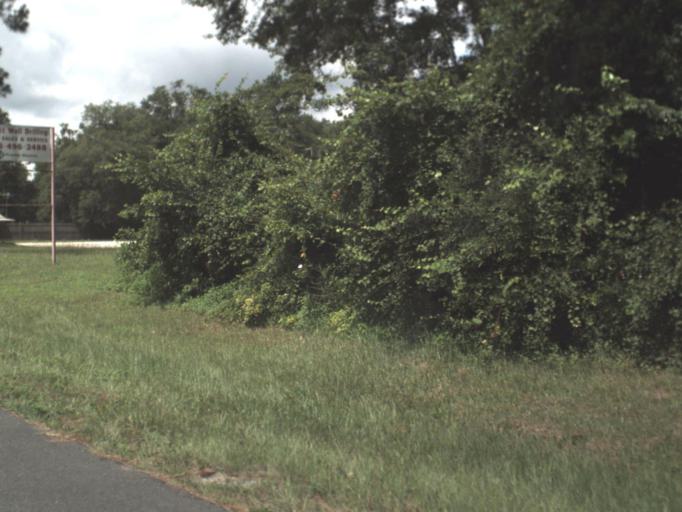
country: US
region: Florida
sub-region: Union County
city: Lake Butler
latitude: 29.9627
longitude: -82.4093
